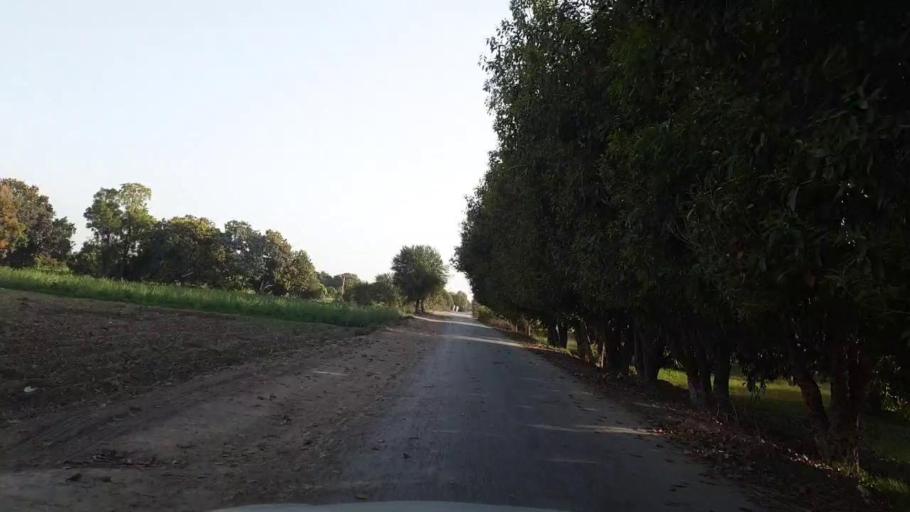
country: PK
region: Sindh
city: Tando Ghulam Ali
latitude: 25.1263
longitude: 68.9069
